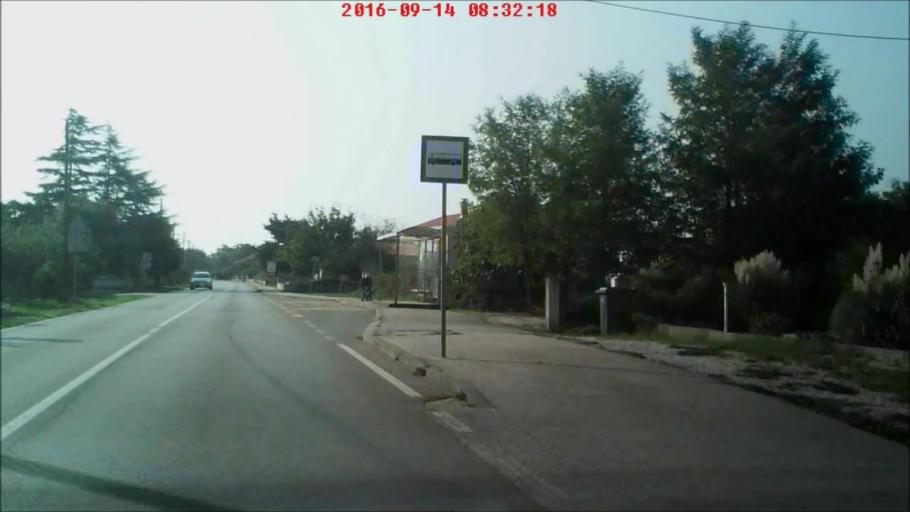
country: HR
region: Zadarska
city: Policnik
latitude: 44.1642
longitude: 15.3054
